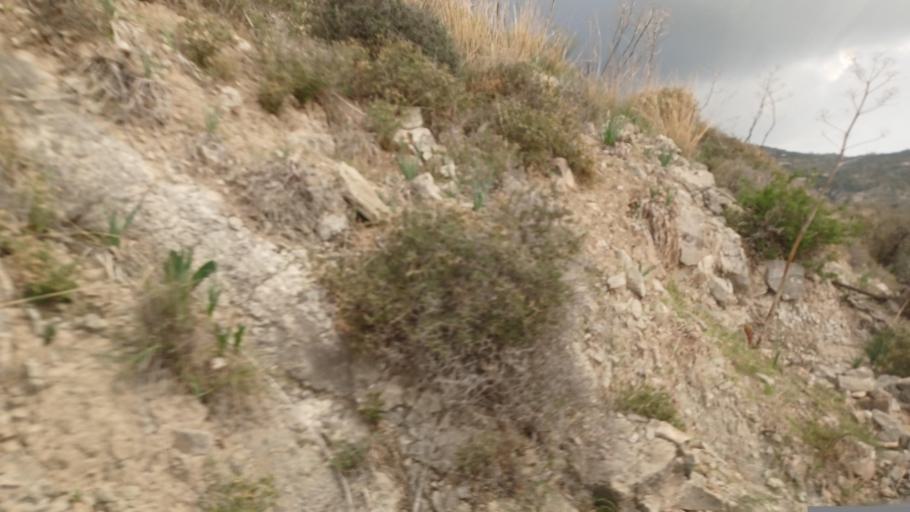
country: CY
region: Pafos
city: Mesogi
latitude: 34.7849
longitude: 32.5167
